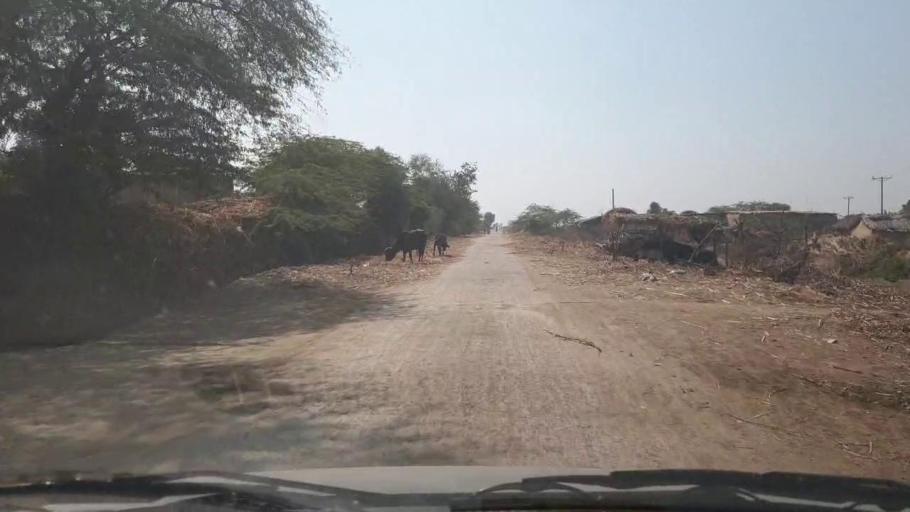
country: PK
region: Sindh
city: Samaro
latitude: 25.2603
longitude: 69.3514
